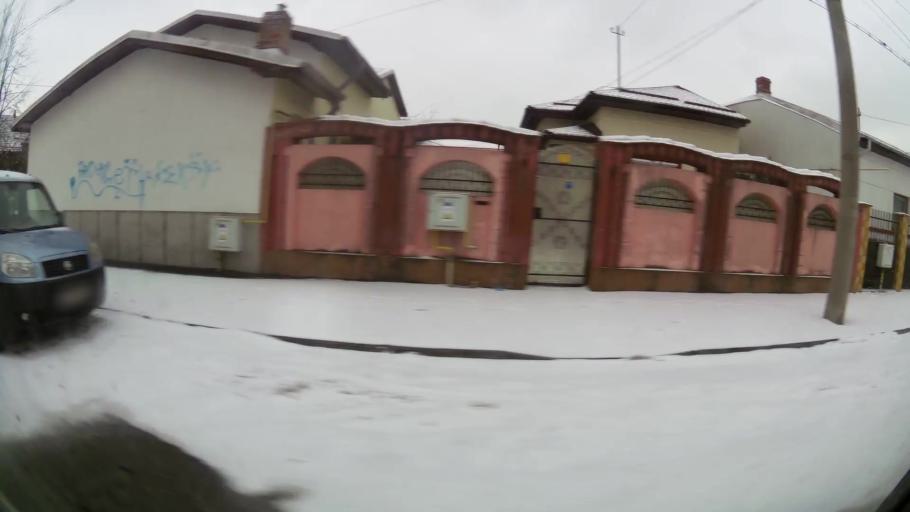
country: RO
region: Prahova
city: Ploiesti
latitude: 44.9371
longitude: 26.0390
